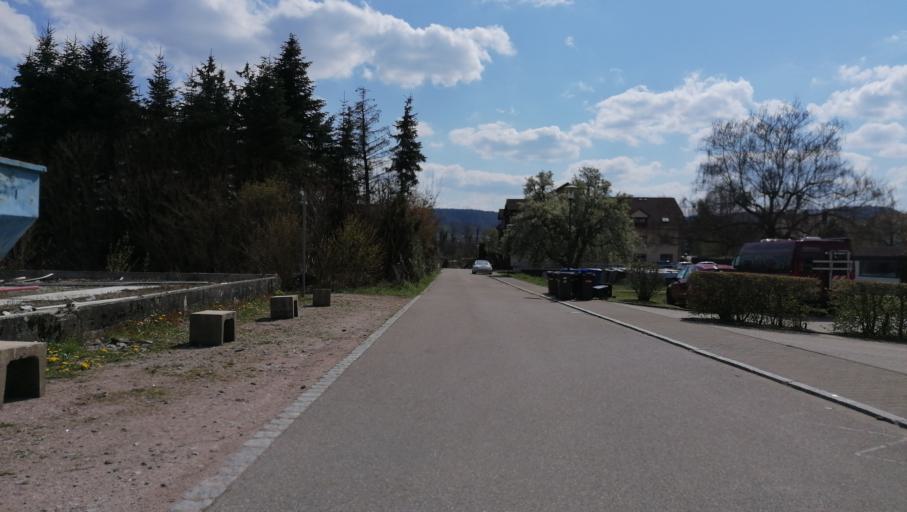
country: CH
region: Aargau
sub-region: Bezirk Rheinfelden
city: Stein
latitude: 47.5587
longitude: 7.9735
